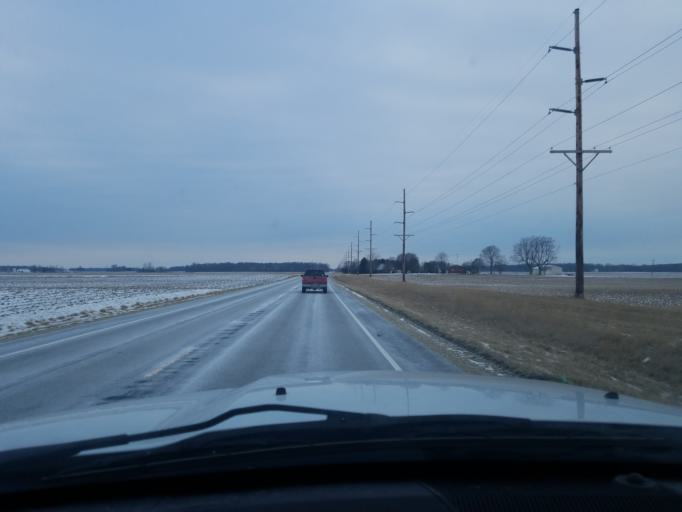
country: US
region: Indiana
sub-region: Randolph County
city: Farmland
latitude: 40.1713
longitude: -85.0708
